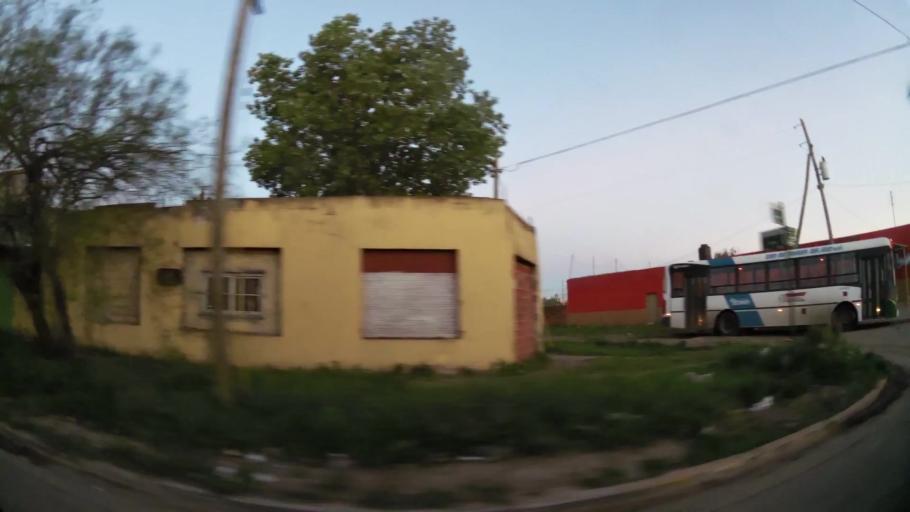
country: AR
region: Buenos Aires
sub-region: Partido de Almirante Brown
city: Adrogue
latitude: -34.7846
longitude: -58.3237
